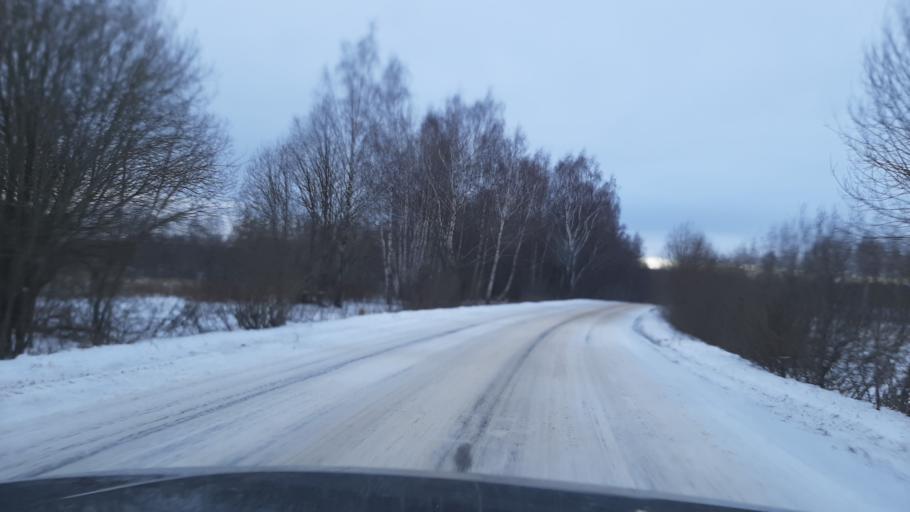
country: RU
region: Kostroma
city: Volgorechensk
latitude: 57.4381
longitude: 41.0467
